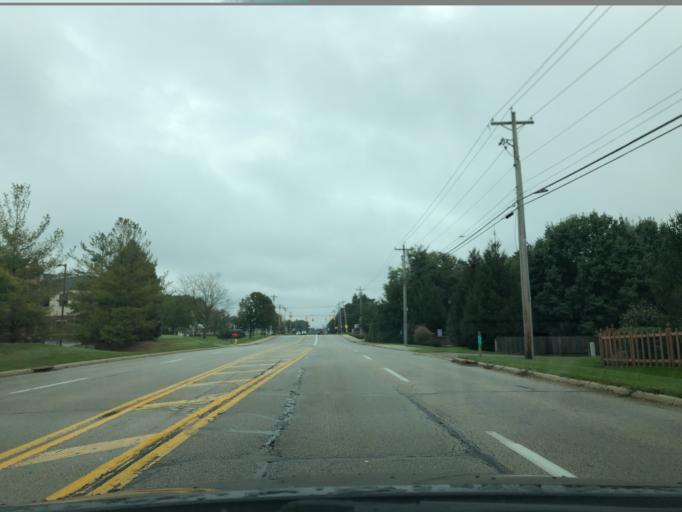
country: US
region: Ohio
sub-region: Hamilton County
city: Sixteen Mile Stand
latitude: 39.2767
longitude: -84.3382
